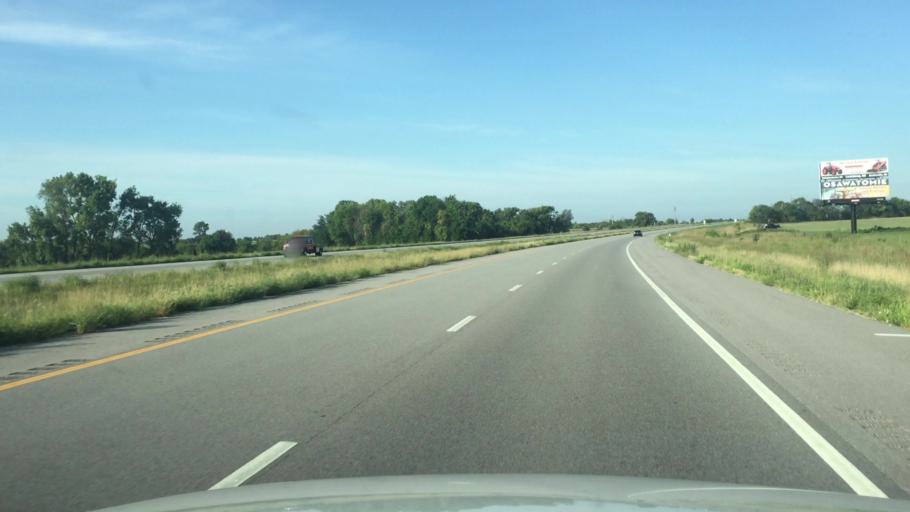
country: US
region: Kansas
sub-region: Miami County
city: Paola
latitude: 38.5303
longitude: -94.8943
